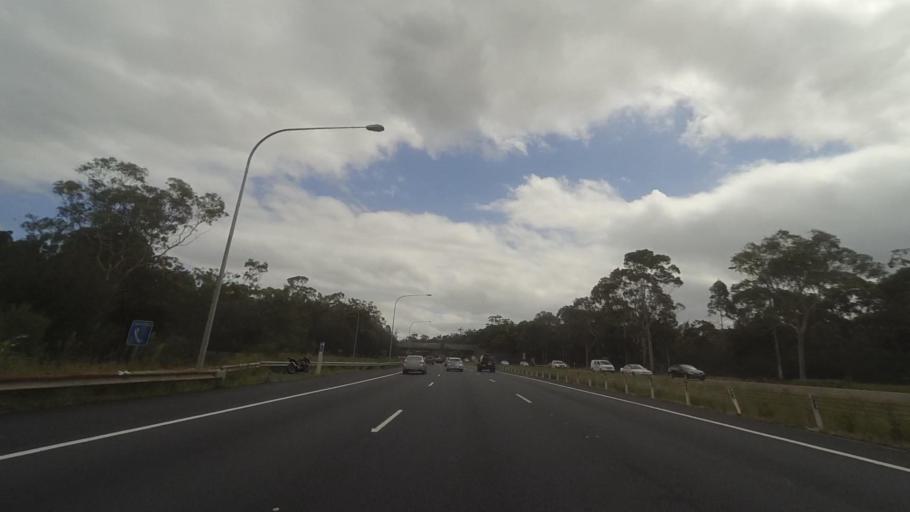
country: AU
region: New South Wales
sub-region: Gosford Shire
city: Umina
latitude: -33.4624
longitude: 151.1964
